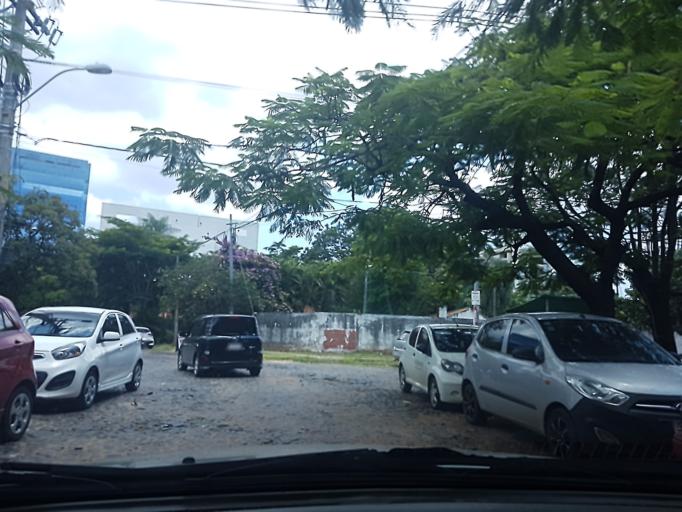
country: PY
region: Central
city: Fernando de la Mora
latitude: -25.2807
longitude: -57.5639
